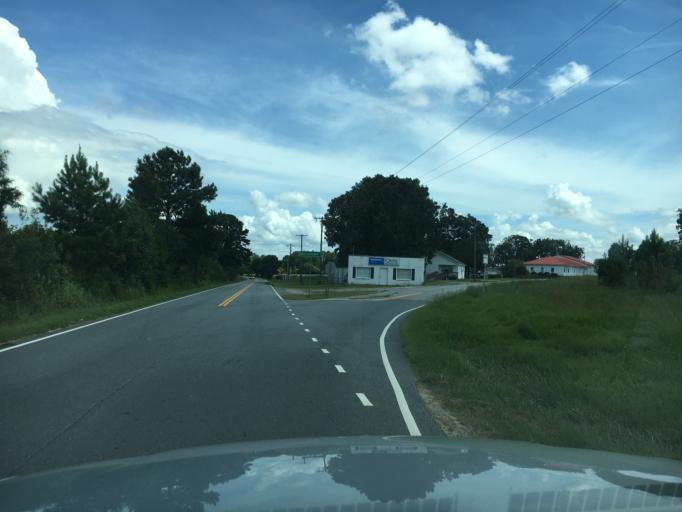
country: US
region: South Carolina
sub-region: Anderson County
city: Honea Path
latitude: 34.5119
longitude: -82.4110
